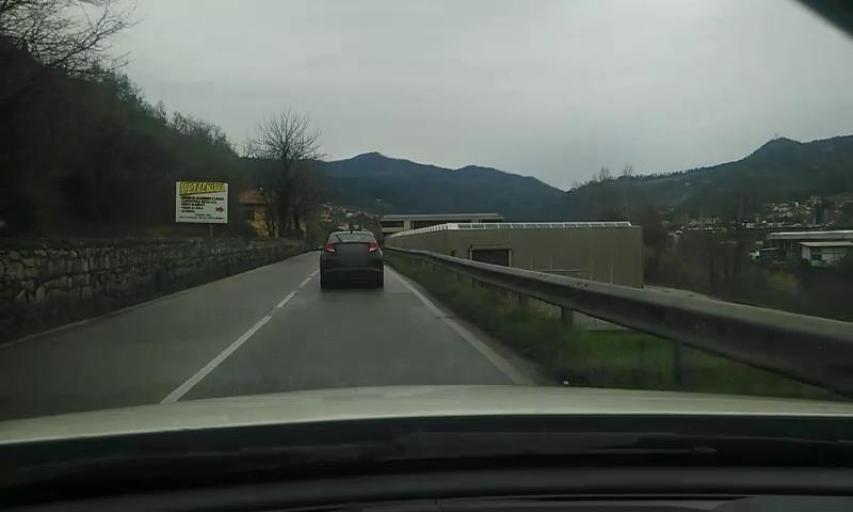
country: IT
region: Tuscany
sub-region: Provincia di Prato
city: Vaiano
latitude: 43.9529
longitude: 11.1271
